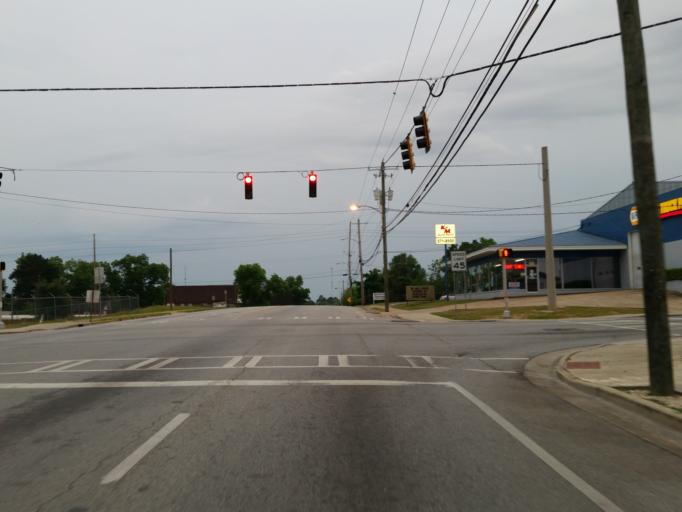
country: US
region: Georgia
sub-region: Crisp County
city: Cordele
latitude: 31.9551
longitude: -83.7825
